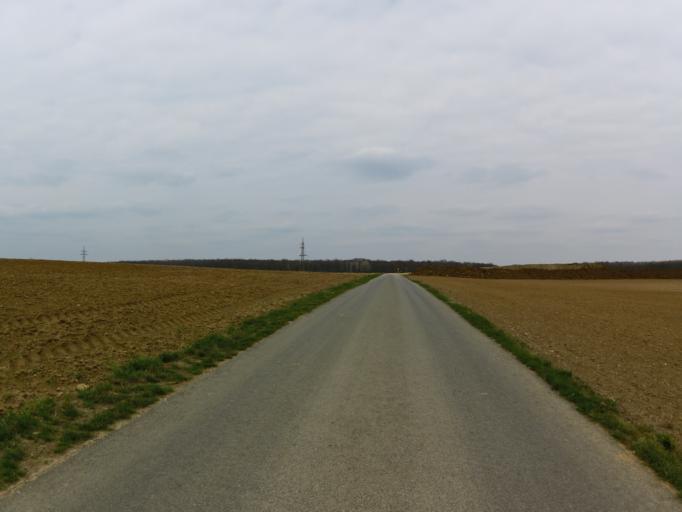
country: DE
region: Bavaria
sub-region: Regierungsbezirk Unterfranken
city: Rottendorf
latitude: 49.8017
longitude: 10.0290
